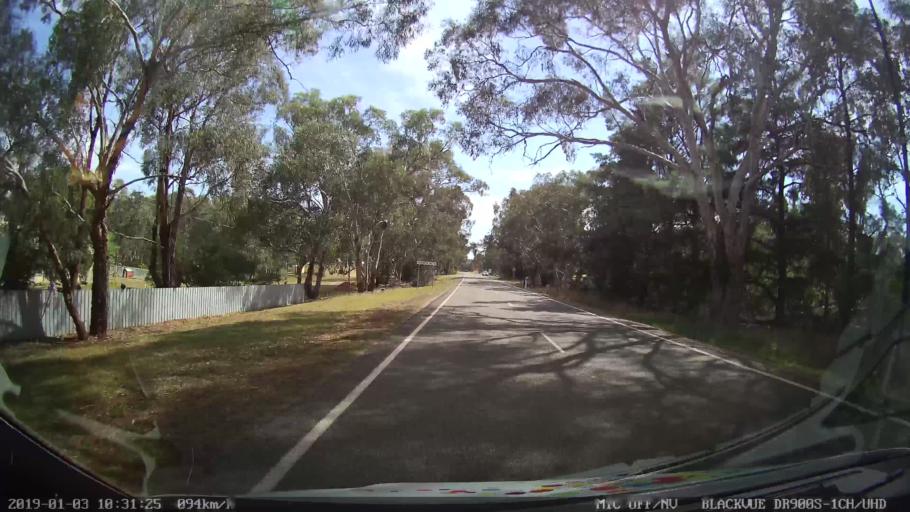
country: AU
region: New South Wales
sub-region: Young
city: Young
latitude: -34.3504
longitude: 148.2771
